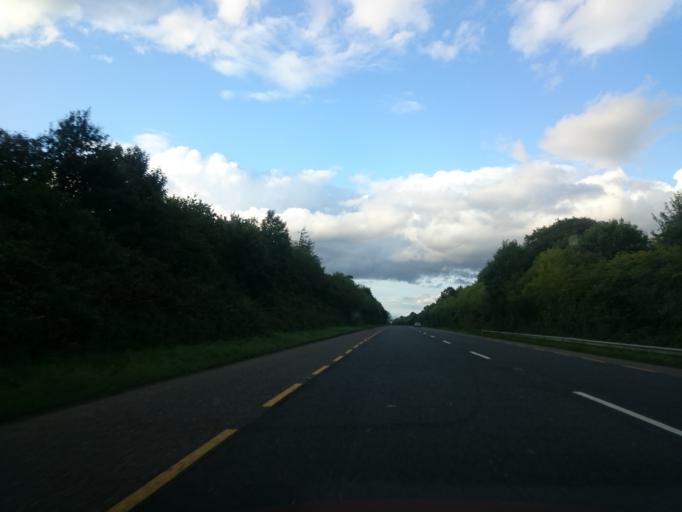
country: IE
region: Leinster
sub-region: Loch Garman
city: Enniscorthy
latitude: 52.5253
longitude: -6.5609
